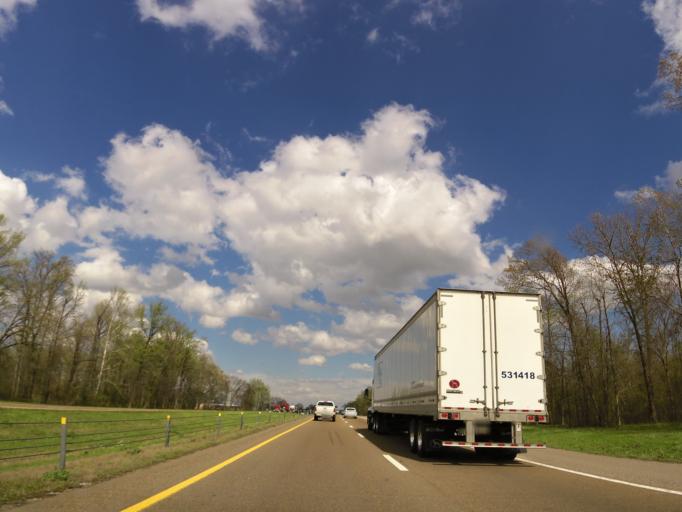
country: US
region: Tennessee
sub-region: Madison County
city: Jackson
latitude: 35.6300
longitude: -88.9594
